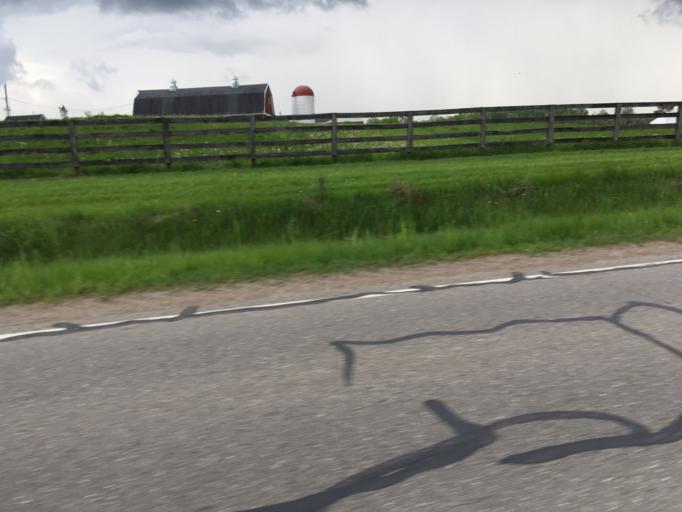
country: US
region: Michigan
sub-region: Lenawee County
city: Clinton
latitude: 42.1593
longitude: -83.9288
